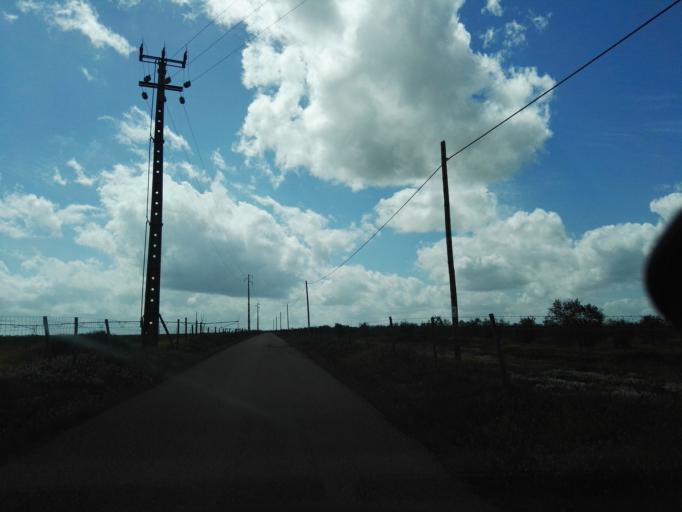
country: PT
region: Portalegre
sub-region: Elvas
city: Elvas
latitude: 38.9521
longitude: -7.1863
